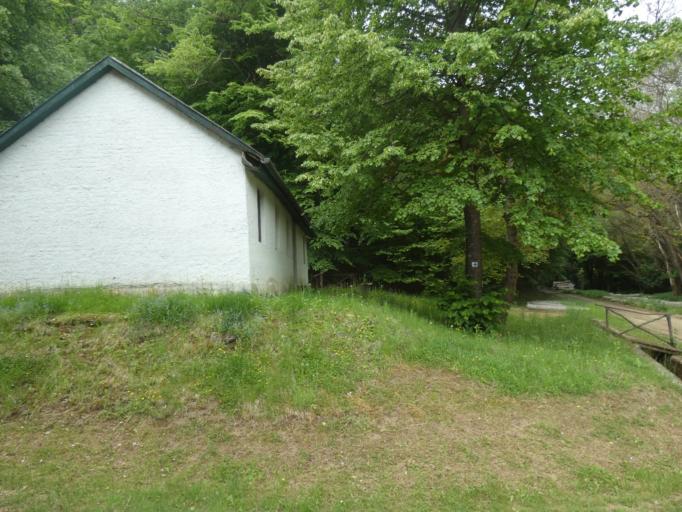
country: HU
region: Heves
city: Petervasara
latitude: 48.1184
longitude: 20.0942
